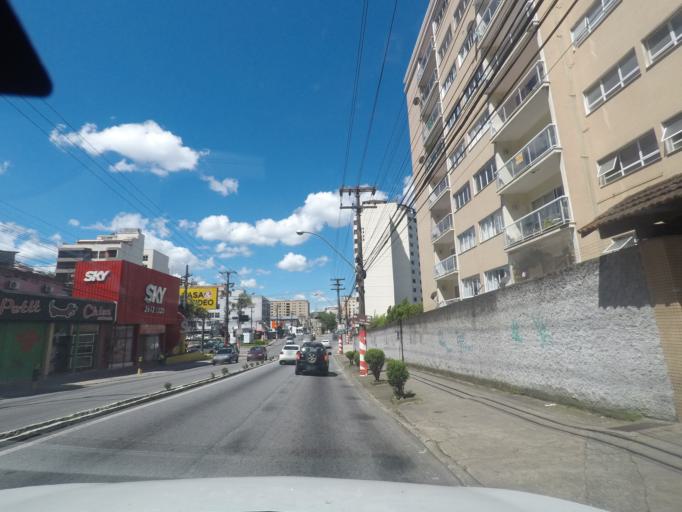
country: BR
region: Rio de Janeiro
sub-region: Teresopolis
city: Teresopolis
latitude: -22.4237
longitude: -42.9779
